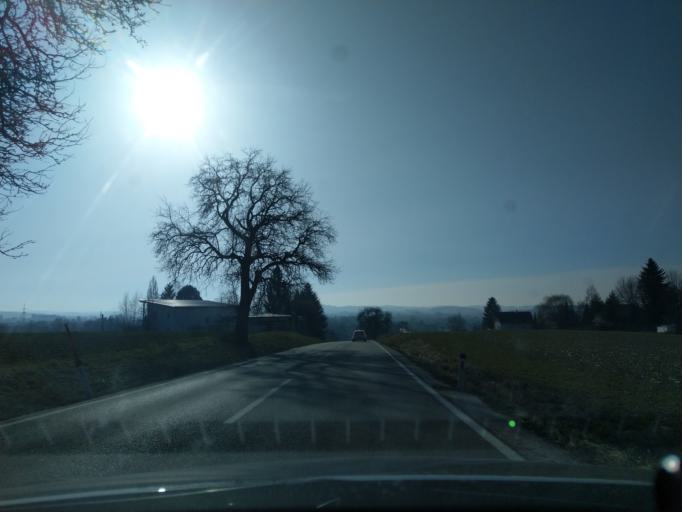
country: AT
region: Upper Austria
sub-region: Politischer Bezirk Ried im Innkreis
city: Ried im Innkreis
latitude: 48.2319
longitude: 13.5037
